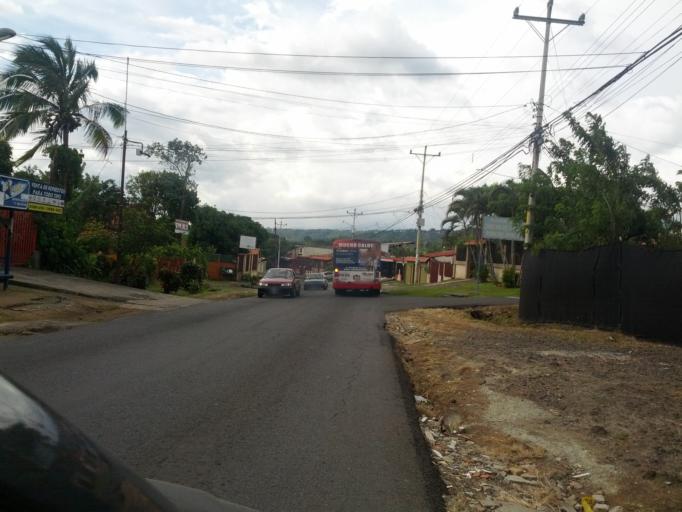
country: CR
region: Alajuela
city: Alajuela
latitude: 10.0266
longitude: -84.1814
